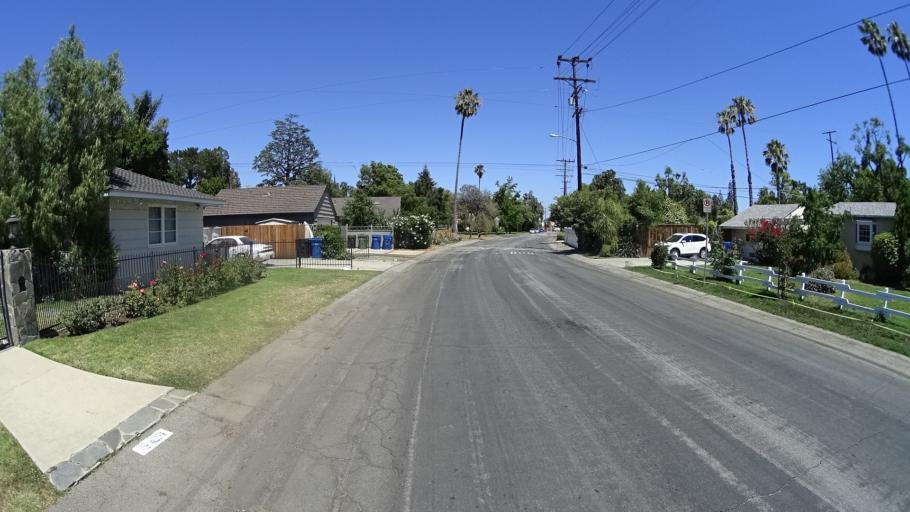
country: US
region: California
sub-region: Los Angeles County
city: Van Nuys
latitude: 34.1892
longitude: -118.4703
